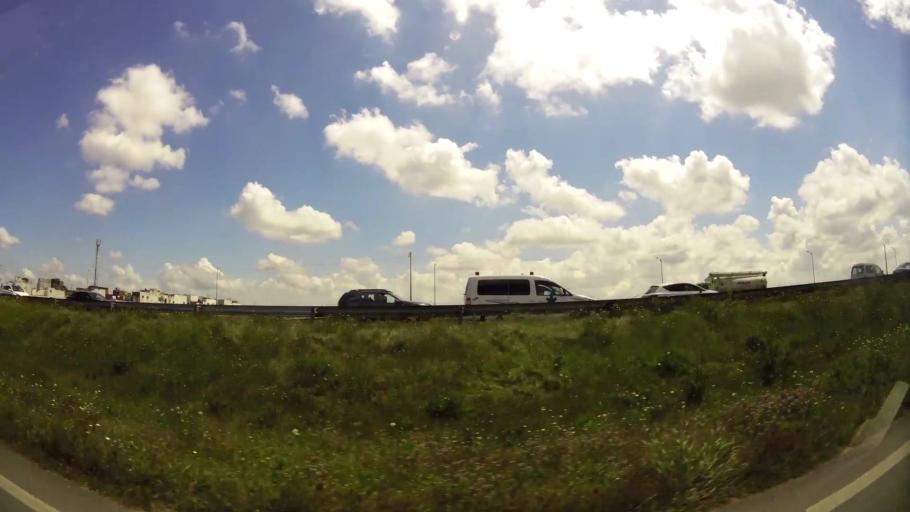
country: MA
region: Grand Casablanca
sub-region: Casablanca
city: Casablanca
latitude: 33.5256
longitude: -7.5709
